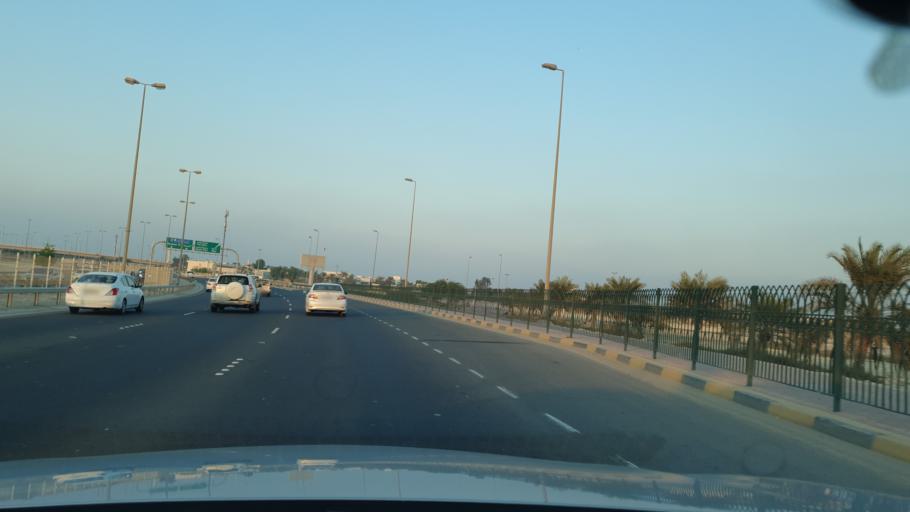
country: BH
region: Northern
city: Madinat `Isa
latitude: 26.1630
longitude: 50.5412
